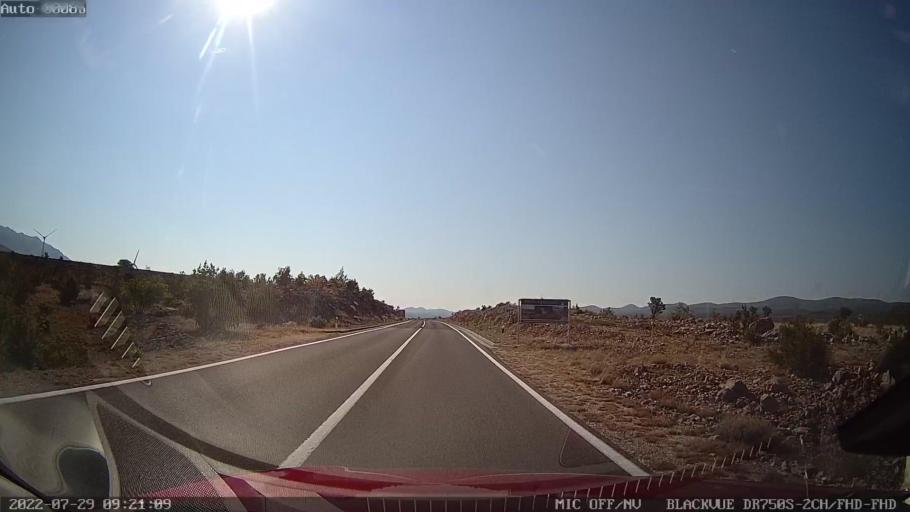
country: HR
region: Zadarska
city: Krusevo
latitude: 44.2223
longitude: 15.6492
